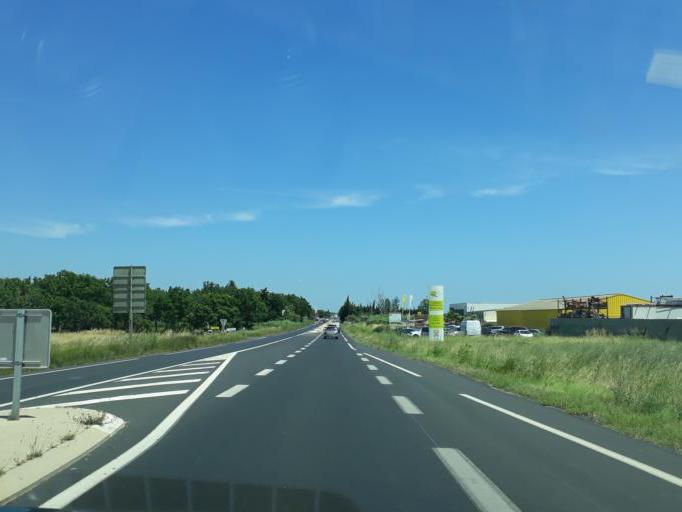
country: FR
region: Languedoc-Roussillon
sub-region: Departement de l'Herault
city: Portiragnes
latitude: 43.3134
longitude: 3.3391
